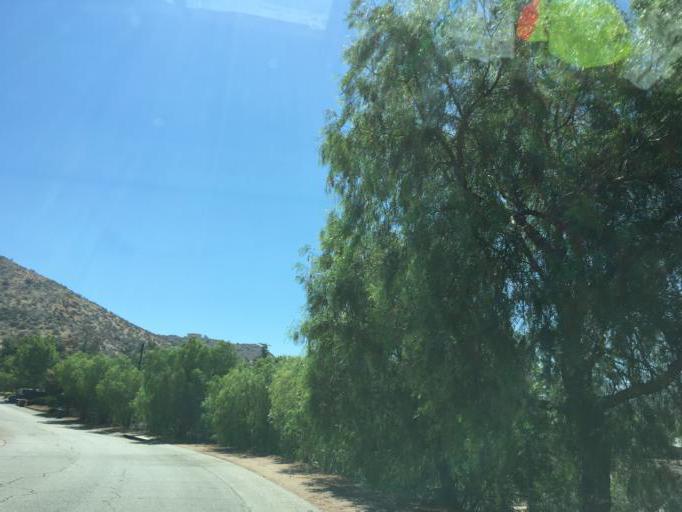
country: US
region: California
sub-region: Los Angeles County
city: Acton
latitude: 34.4929
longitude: -118.1608
